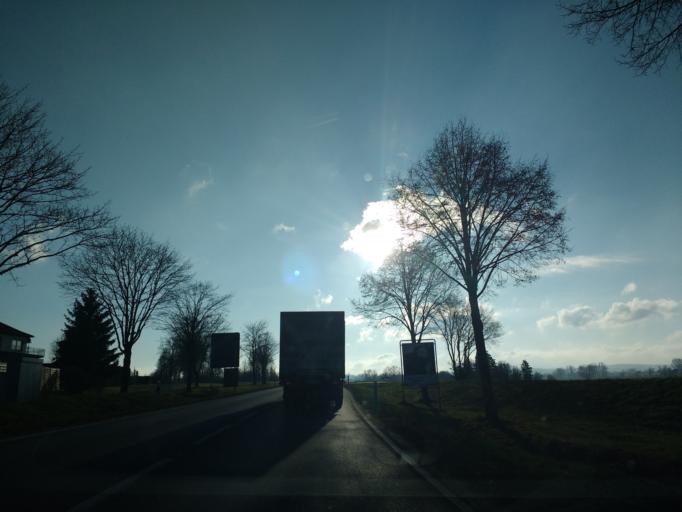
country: DE
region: Hesse
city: Schwalmstadt
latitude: 50.9103
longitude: 9.2537
